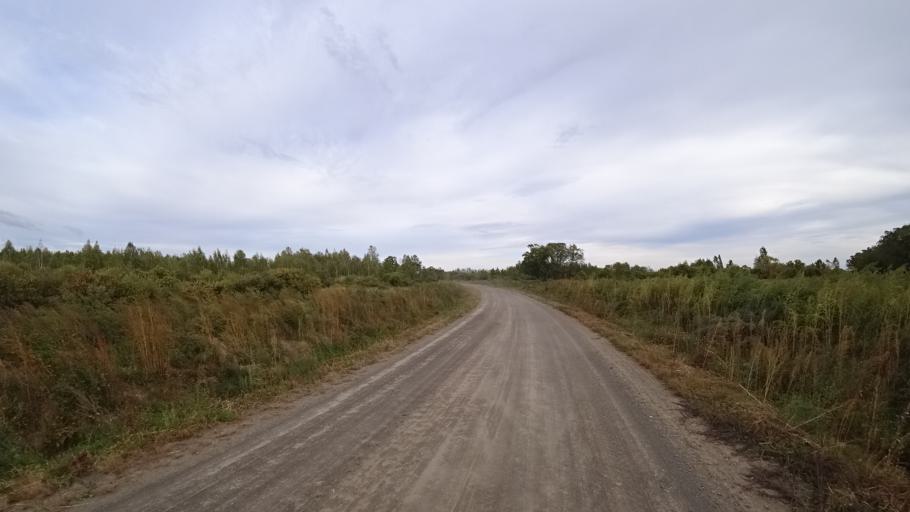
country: RU
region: Amur
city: Arkhara
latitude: 49.3517
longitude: 130.1507
